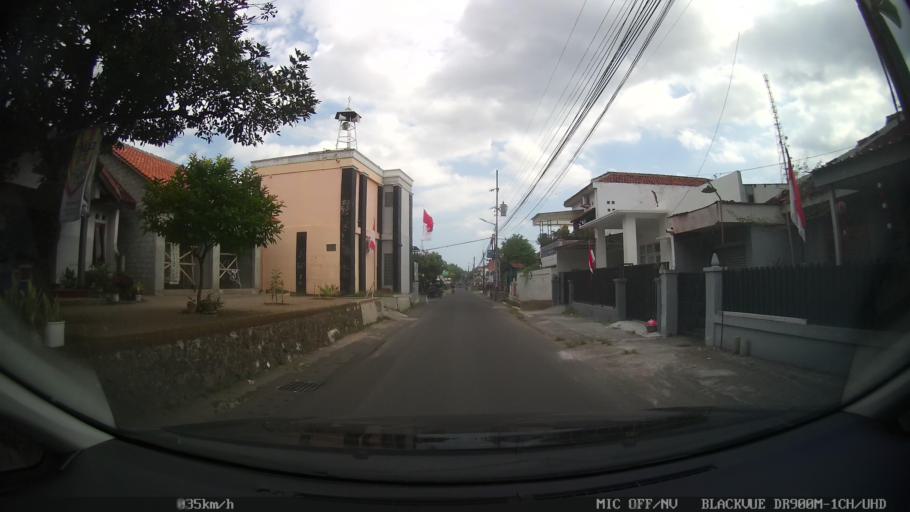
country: ID
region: Daerah Istimewa Yogyakarta
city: Yogyakarta
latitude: -7.7713
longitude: 110.3382
